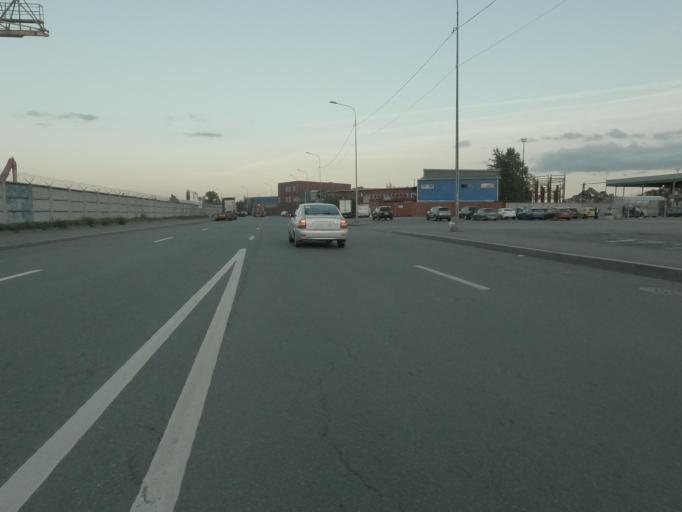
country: RU
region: St.-Petersburg
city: Vasyl'evsky Ostrov
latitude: 59.9040
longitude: 30.2354
